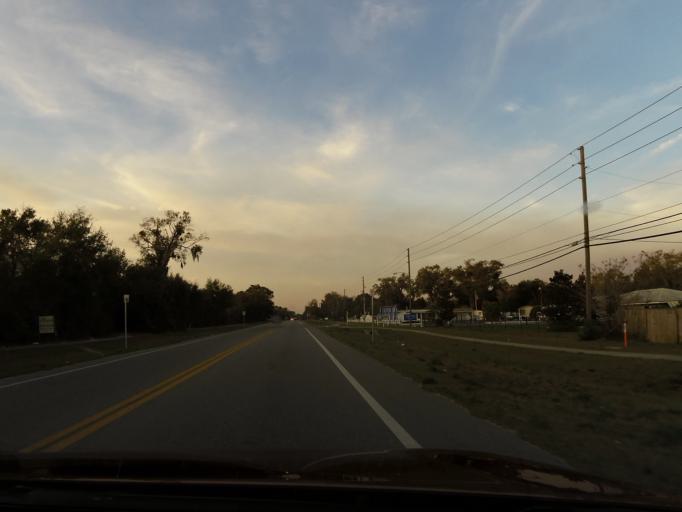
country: US
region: Florida
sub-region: Volusia County
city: North DeLand
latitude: 29.0743
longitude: -81.3048
